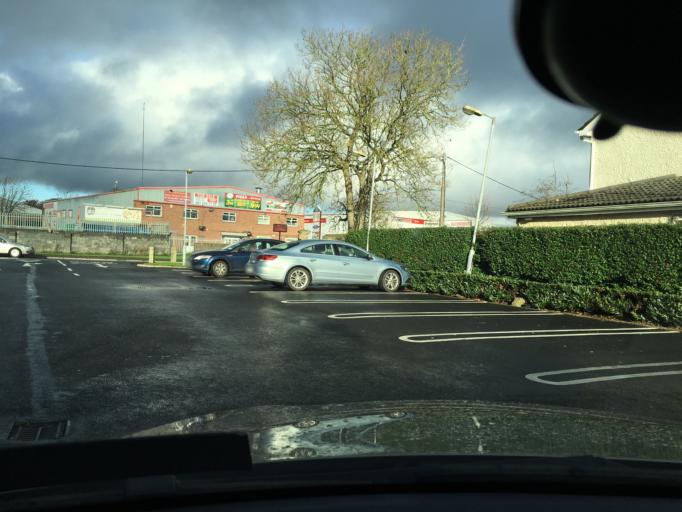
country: IE
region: Leinster
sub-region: Fingal County
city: Blanchardstown
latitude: 53.3824
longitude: -6.3993
